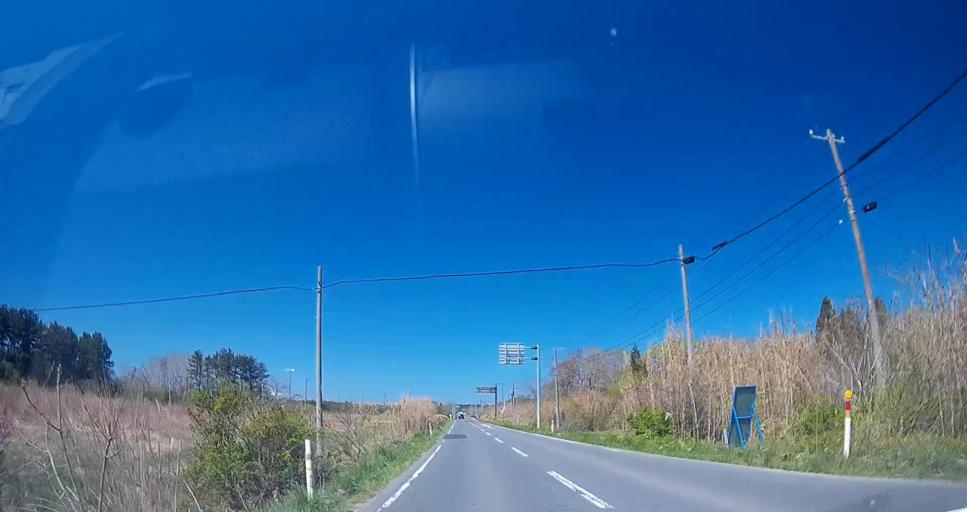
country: JP
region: Aomori
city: Misawa
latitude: 40.8461
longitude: 141.3817
